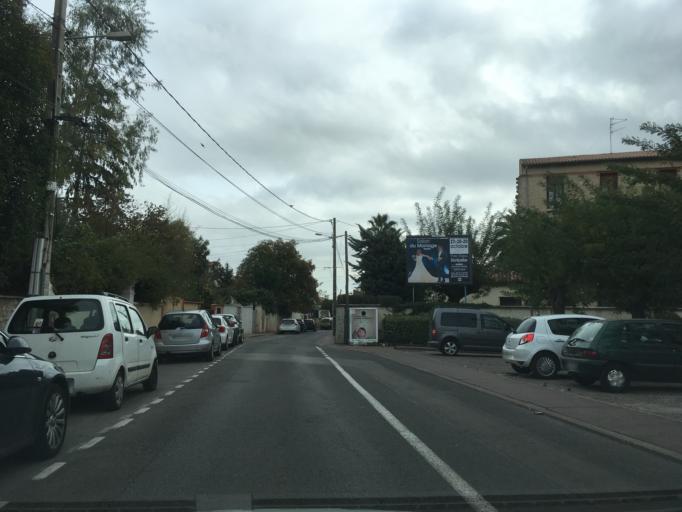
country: FR
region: Languedoc-Roussillon
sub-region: Departement de l'Herault
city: Montpellier
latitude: 43.5960
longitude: 3.8862
